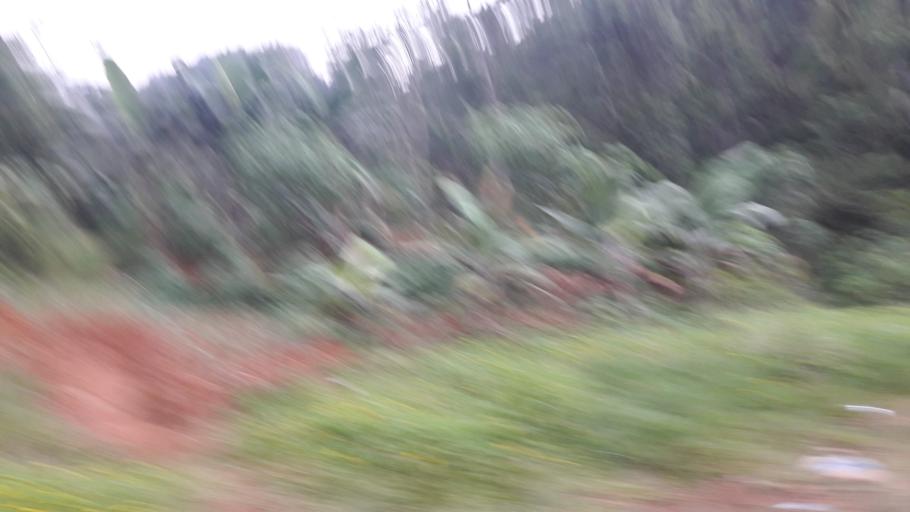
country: ID
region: West Java
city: Cipeundeuy
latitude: -6.6783
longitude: 106.5173
